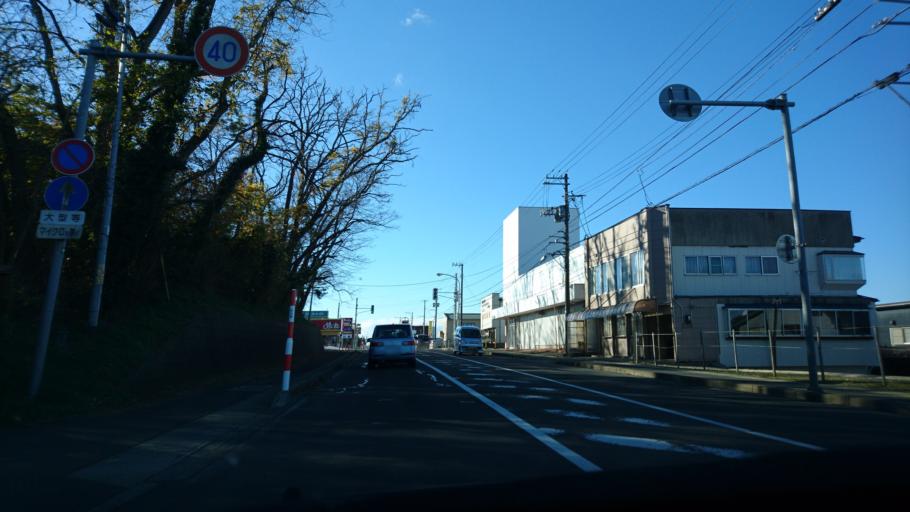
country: JP
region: Akita
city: Akita Shi
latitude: 39.3864
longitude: 140.0385
